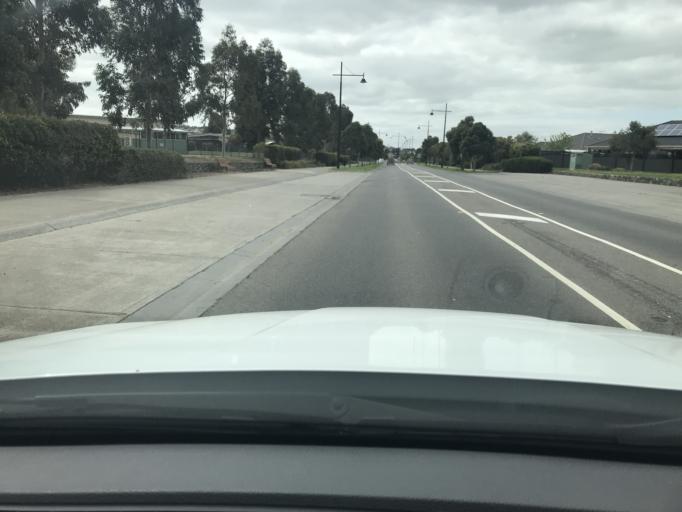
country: AU
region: Victoria
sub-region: Hume
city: Craigieburn
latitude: -37.5807
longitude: 144.9248
